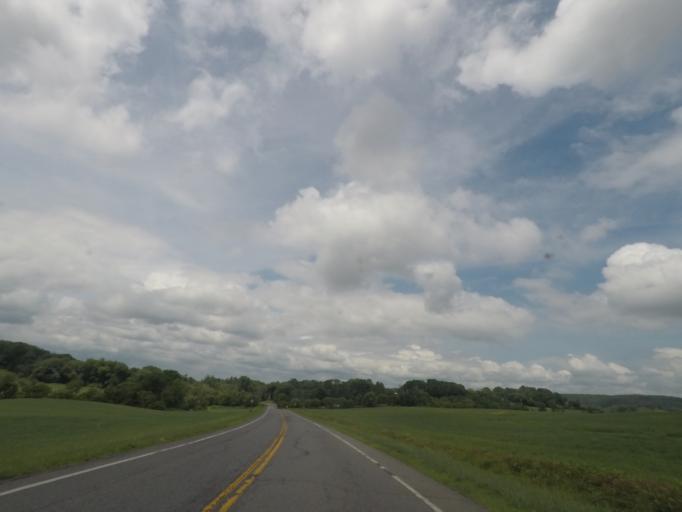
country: US
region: New York
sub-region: Saratoga County
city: Stillwater
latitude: 43.0449
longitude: -73.6778
